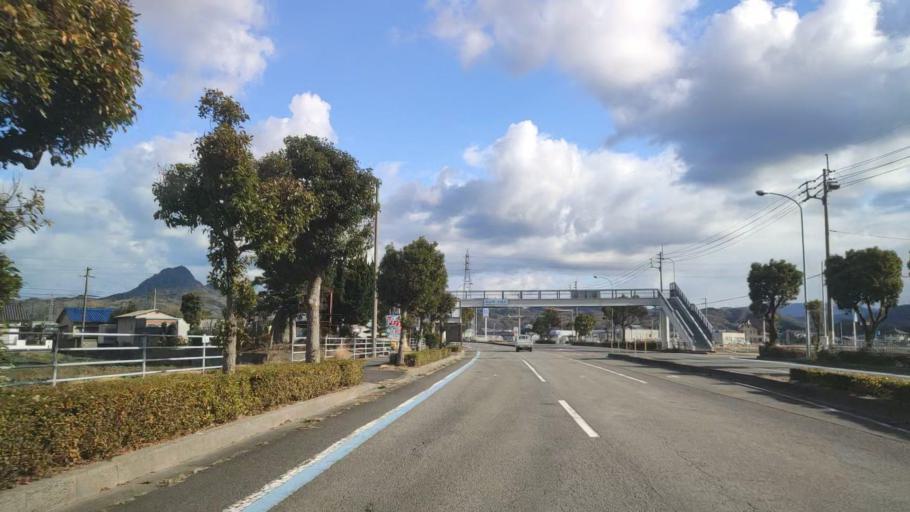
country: JP
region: Ehime
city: Hojo
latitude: 33.9683
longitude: 132.7812
